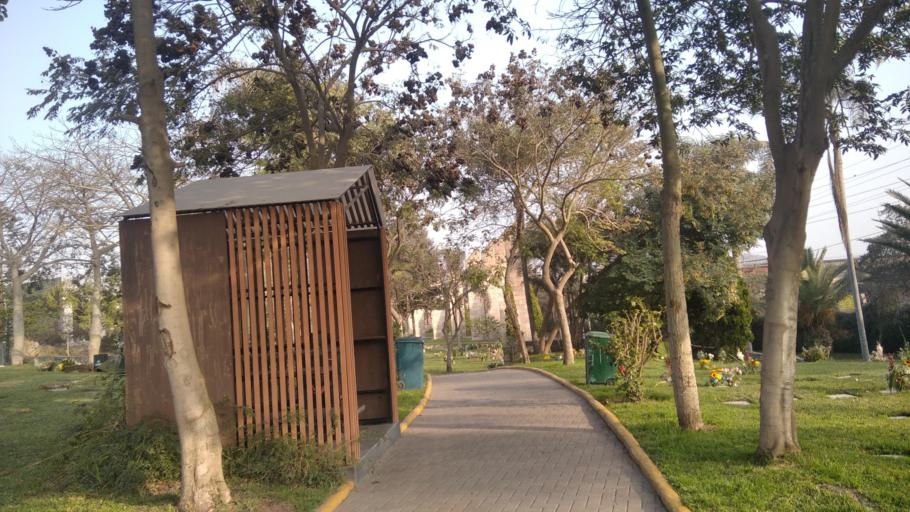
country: PE
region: Lima
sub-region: Lima
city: Santa Maria
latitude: -12.0092
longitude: -76.9132
